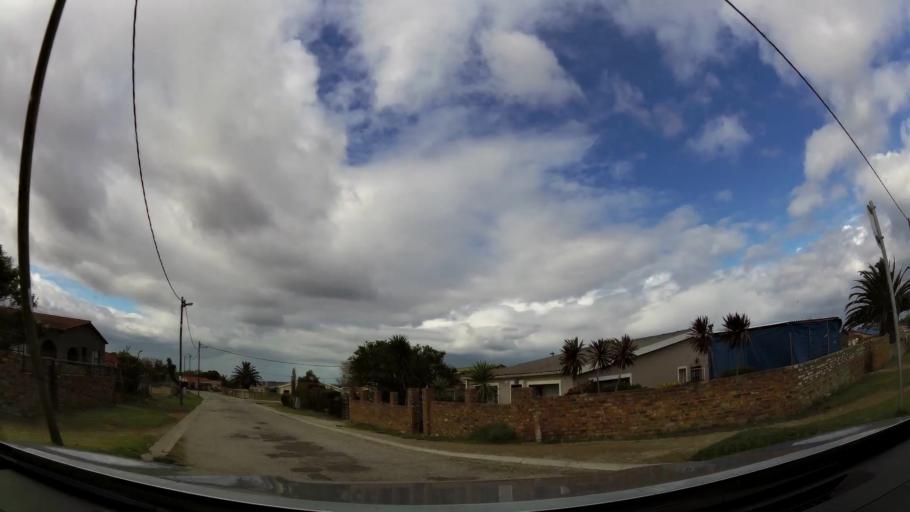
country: ZA
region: Western Cape
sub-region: Eden District Municipality
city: George
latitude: -34.0204
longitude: 22.4710
